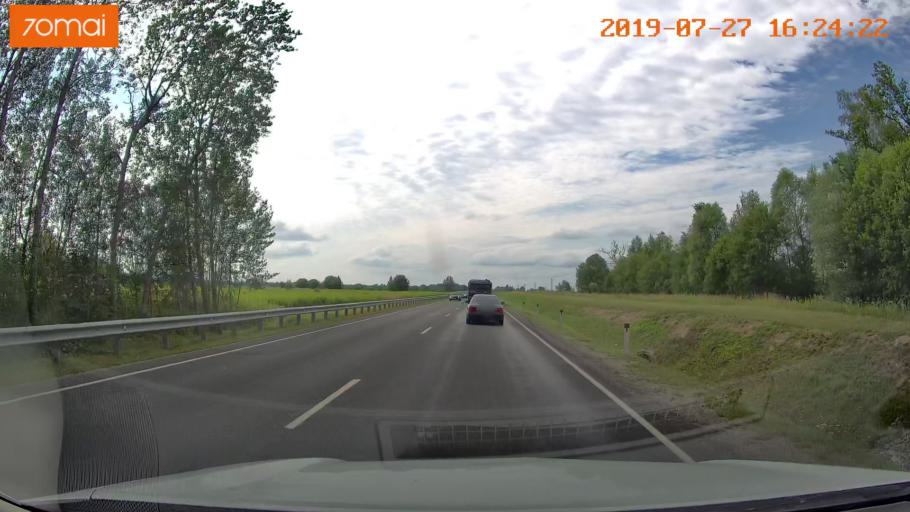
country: RU
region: Kaliningrad
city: Zheleznodorozhnyy
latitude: 54.6339
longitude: 21.4540
